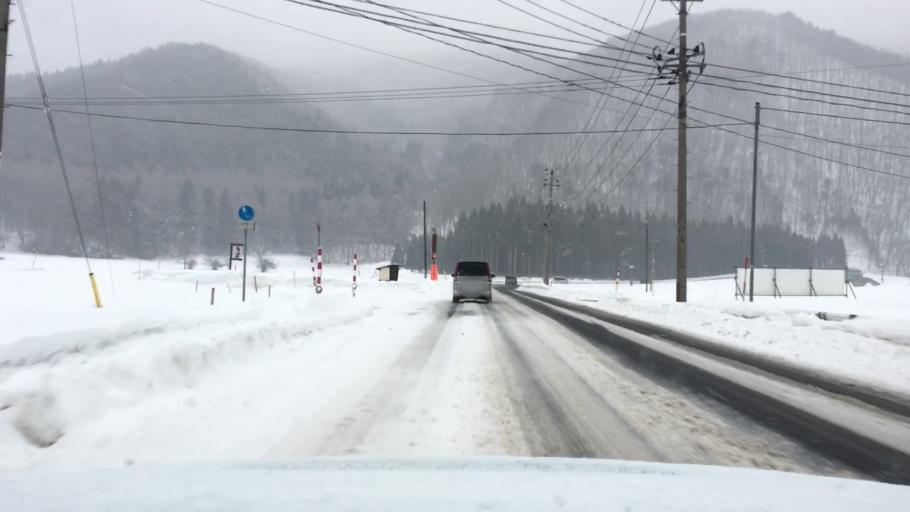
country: JP
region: Akita
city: Hanawa
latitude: 40.0791
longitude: 141.0228
